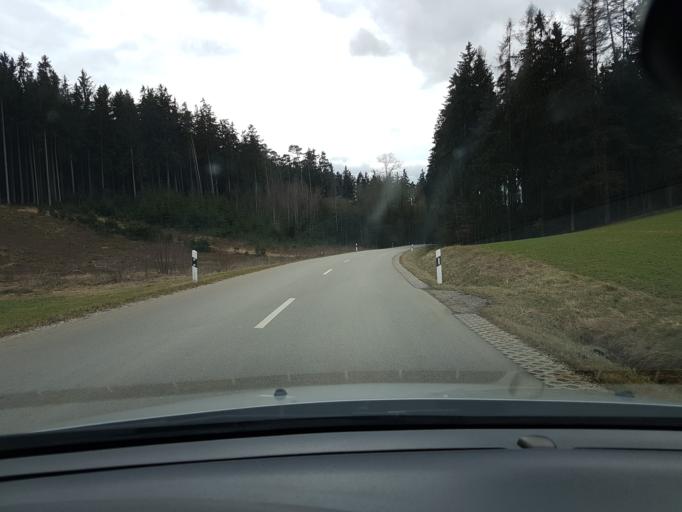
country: DE
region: Bavaria
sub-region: Lower Bavaria
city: Kumhausen
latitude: 48.5062
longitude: 12.2052
